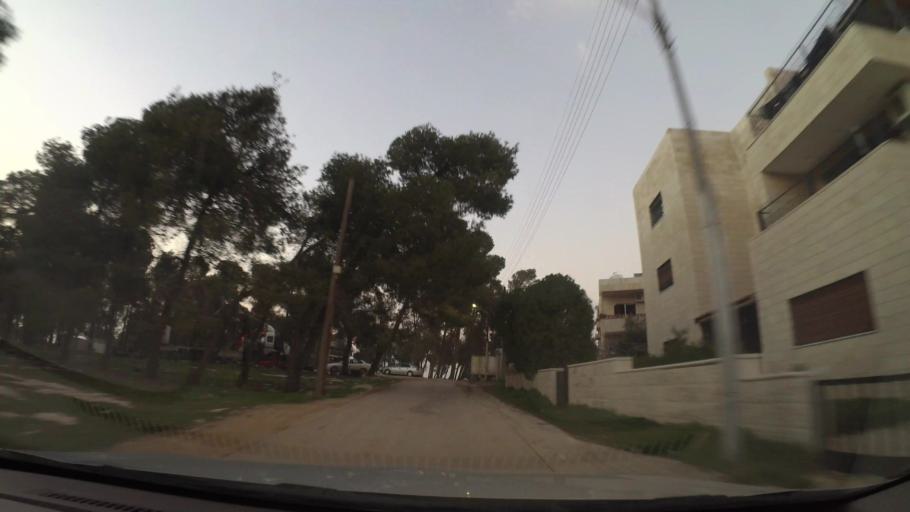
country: JO
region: Amman
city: Al Bunayyat ash Shamaliyah
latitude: 31.8911
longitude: 35.9207
